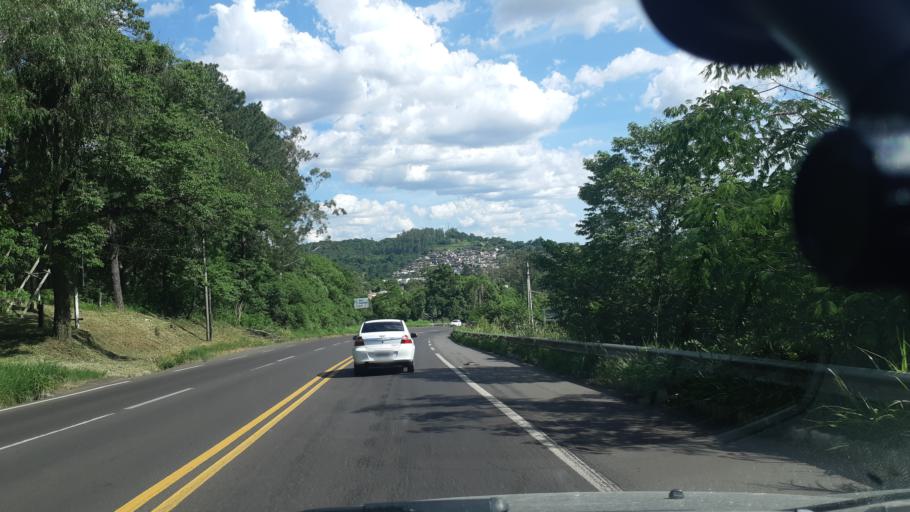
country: BR
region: Rio Grande do Sul
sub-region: Estancia Velha
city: Estancia Velha
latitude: -29.6364
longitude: -51.1422
